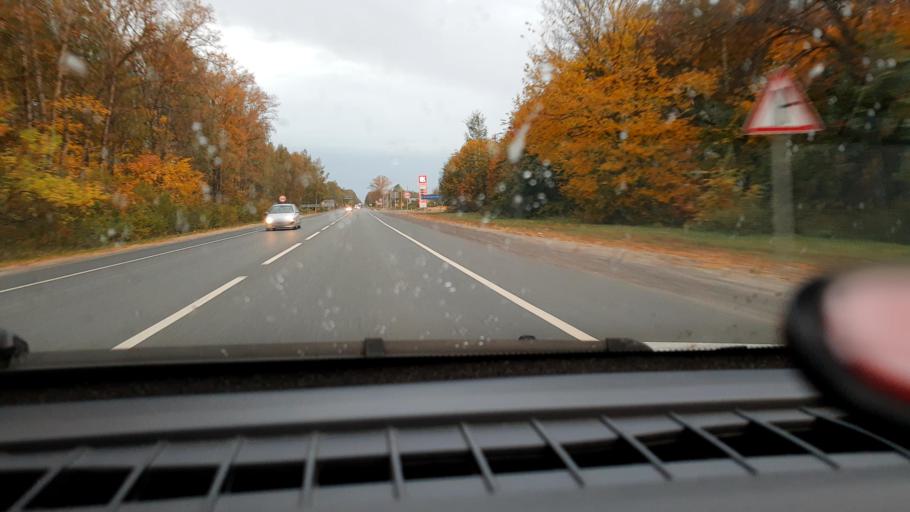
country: RU
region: Vladimir
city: Orgtrud
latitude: 56.2029
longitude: 40.7635
